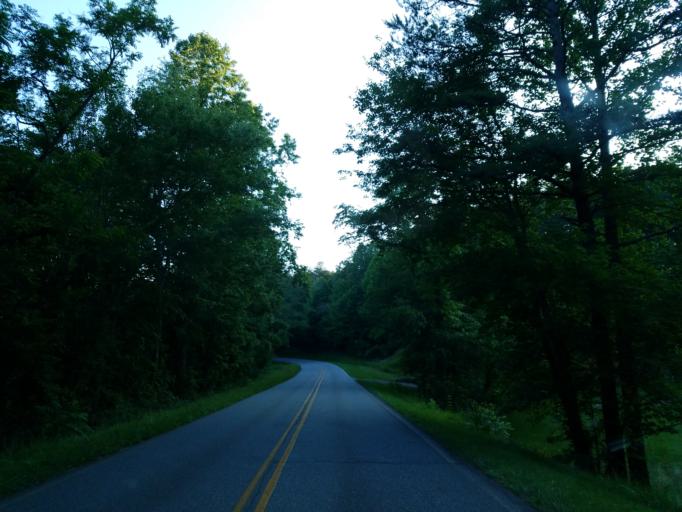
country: US
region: Georgia
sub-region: Fannin County
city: Blue Ridge
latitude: 34.7986
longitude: -84.1573
